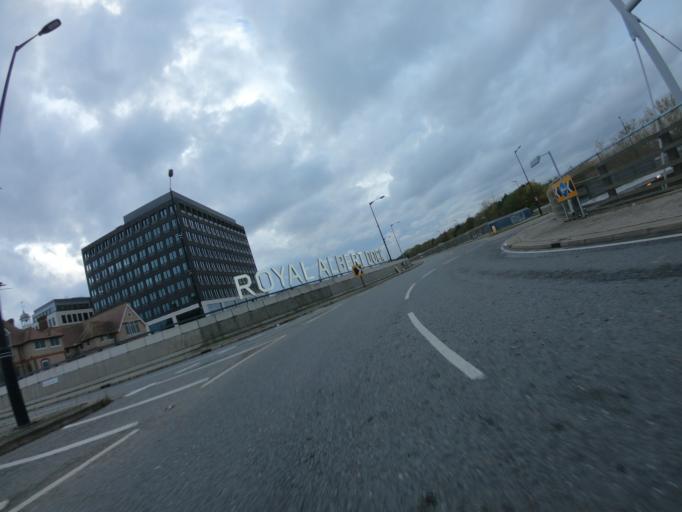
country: GB
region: England
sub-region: Greater London
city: Woolwich
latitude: 51.5086
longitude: 0.0550
